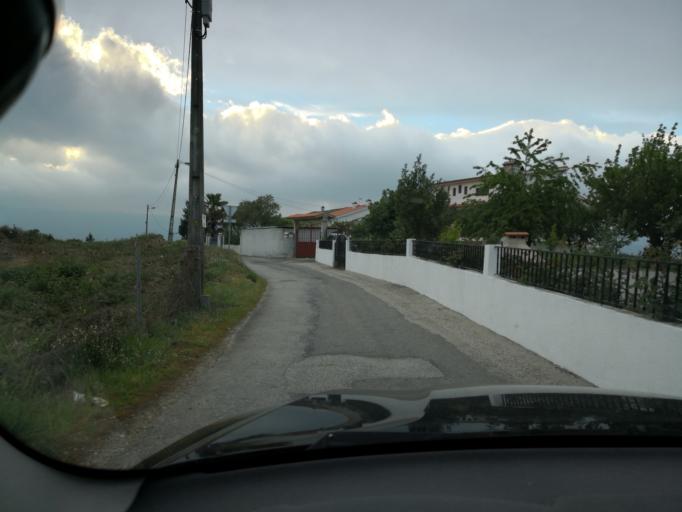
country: PT
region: Vila Real
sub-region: Vila Real
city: Vila Real
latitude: 41.2785
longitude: -7.7249
